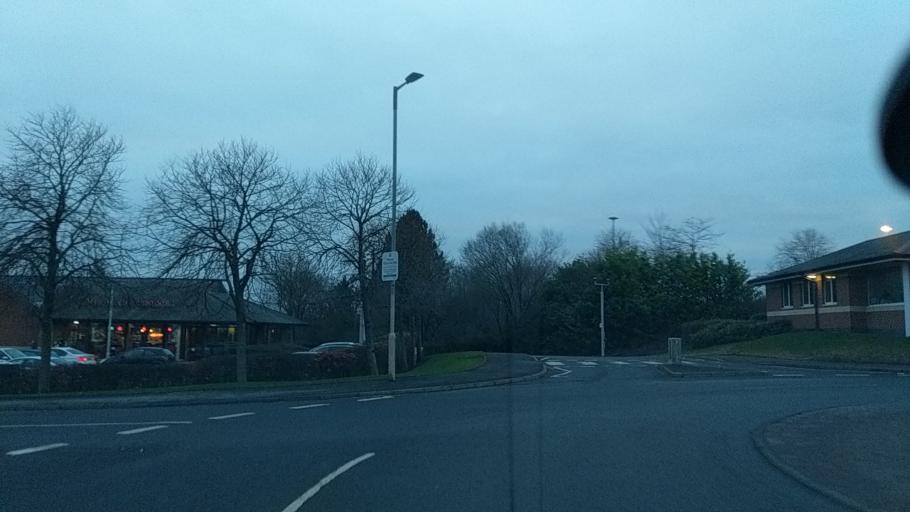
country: GB
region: Scotland
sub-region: South Lanarkshire
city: East Kilbride
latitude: 55.7832
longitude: -4.1675
